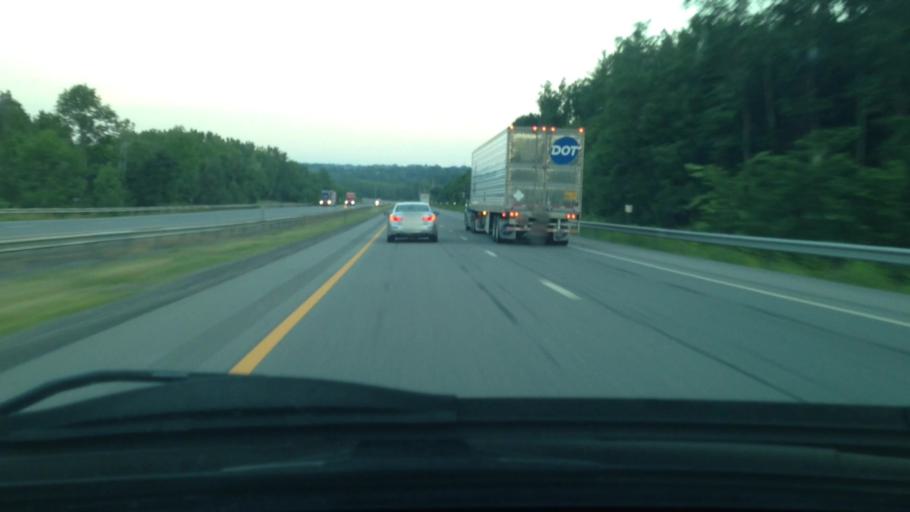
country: US
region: New York
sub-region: Montgomery County
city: Fort Plain
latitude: 42.9489
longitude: -74.6320
